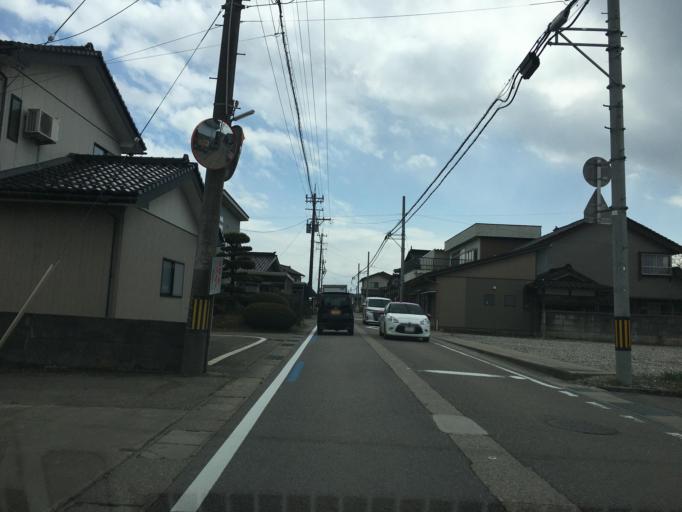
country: JP
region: Toyama
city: Kuragaki-kosugi
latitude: 36.6931
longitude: 137.1165
